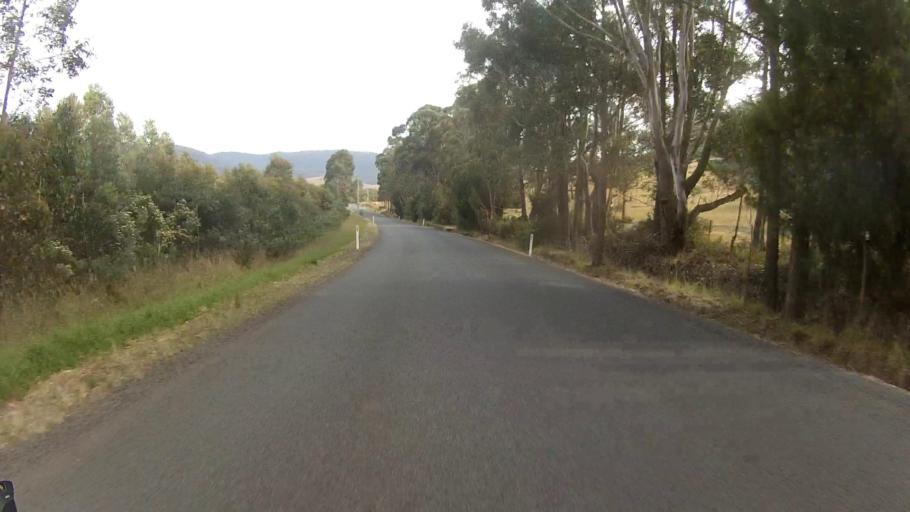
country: AU
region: Tasmania
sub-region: Sorell
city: Sorell
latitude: -42.8080
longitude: 147.7946
